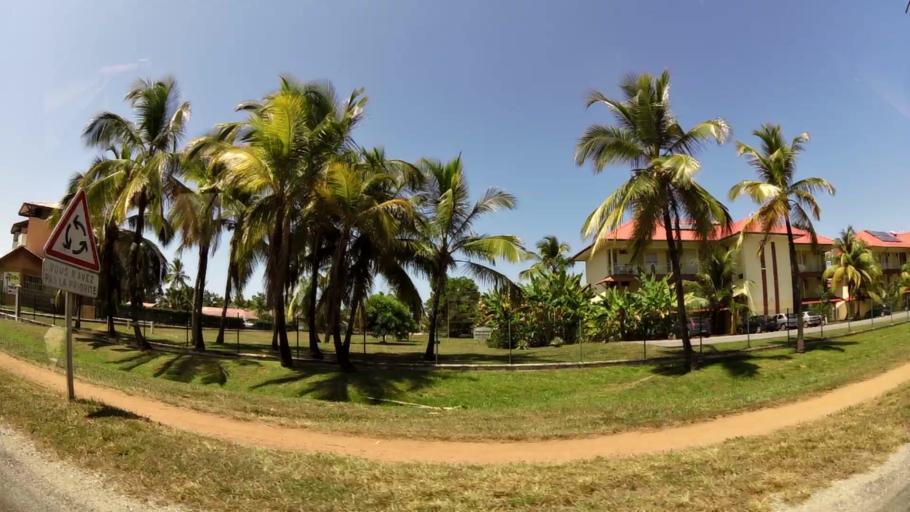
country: GF
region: Guyane
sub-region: Guyane
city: Kourou
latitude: 5.1718
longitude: -52.6494
